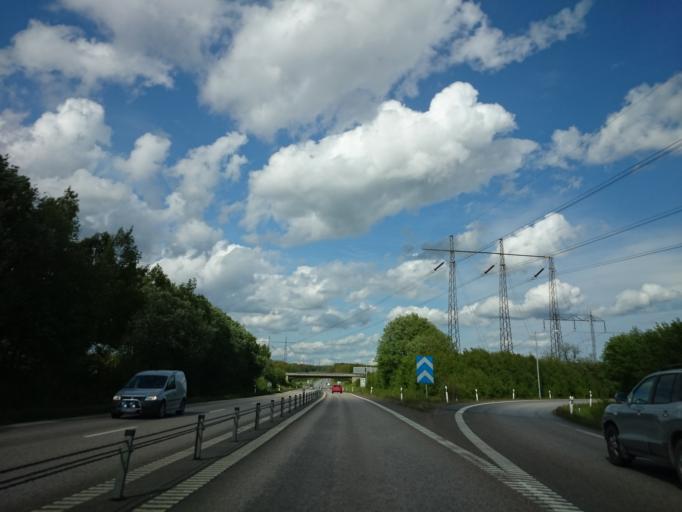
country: SE
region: Skane
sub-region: Horby Kommun
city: Hoerby
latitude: 55.8575
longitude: 13.6372
